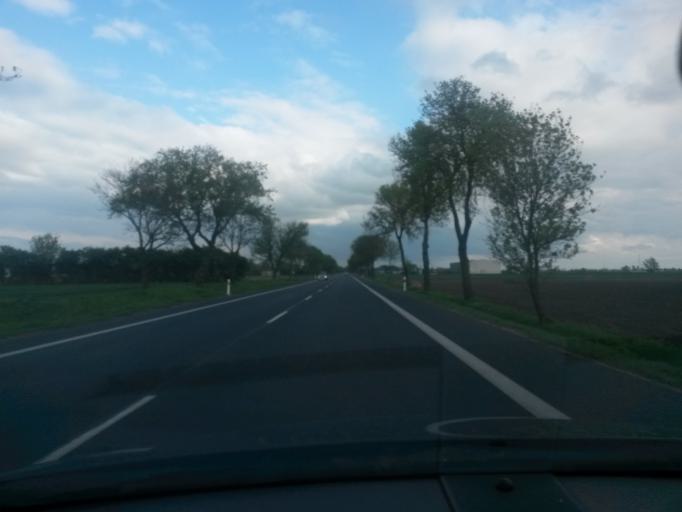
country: PL
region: Masovian Voivodeship
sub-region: Powiat plocki
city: Drobin
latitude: 52.7526
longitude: 19.9660
